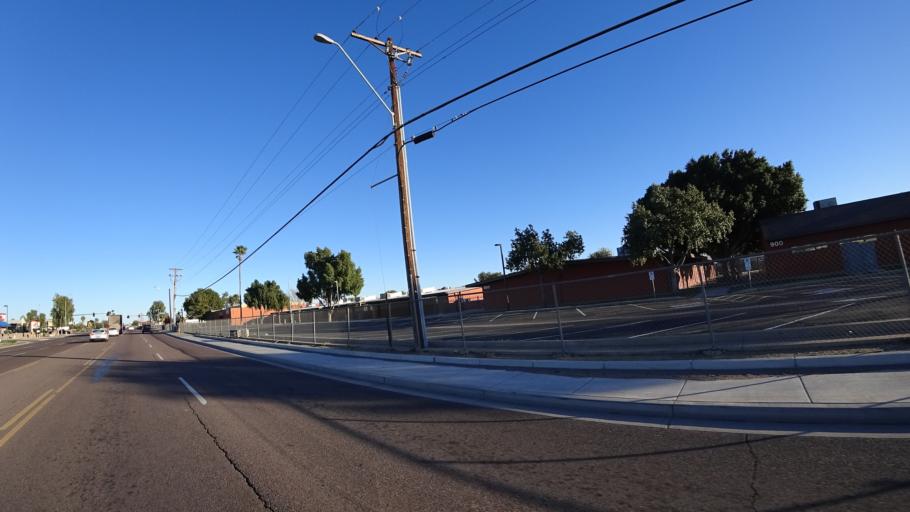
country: US
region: Arizona
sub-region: Maricopa County
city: Tolleson
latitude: 33.4515
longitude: -112.2054
